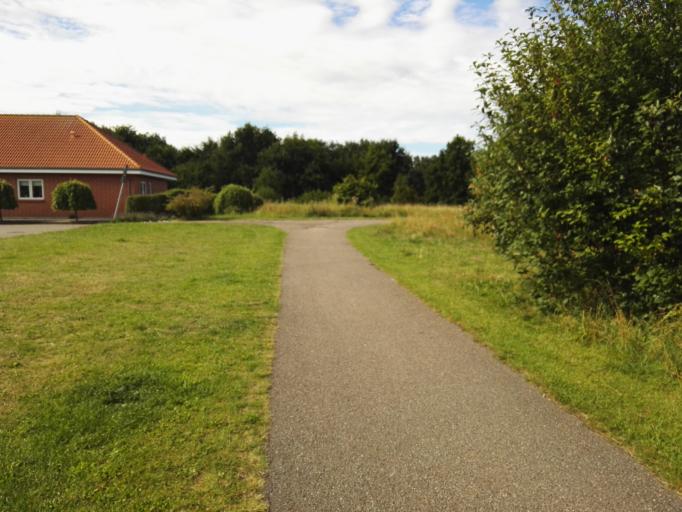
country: DK
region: Zealand
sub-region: Odsherred Kommune
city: Nykobing Sjaelland
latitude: 55.9342
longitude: 11.6734
